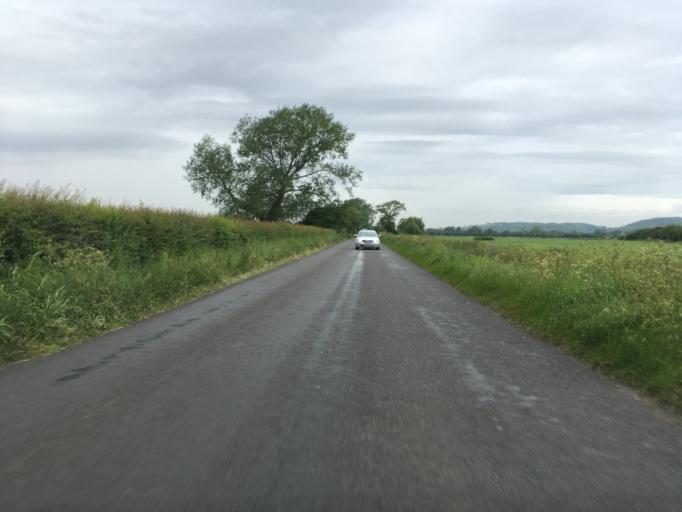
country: GB
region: England
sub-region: North Somerset
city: Yatton
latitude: 51.4215
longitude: -2.8104
